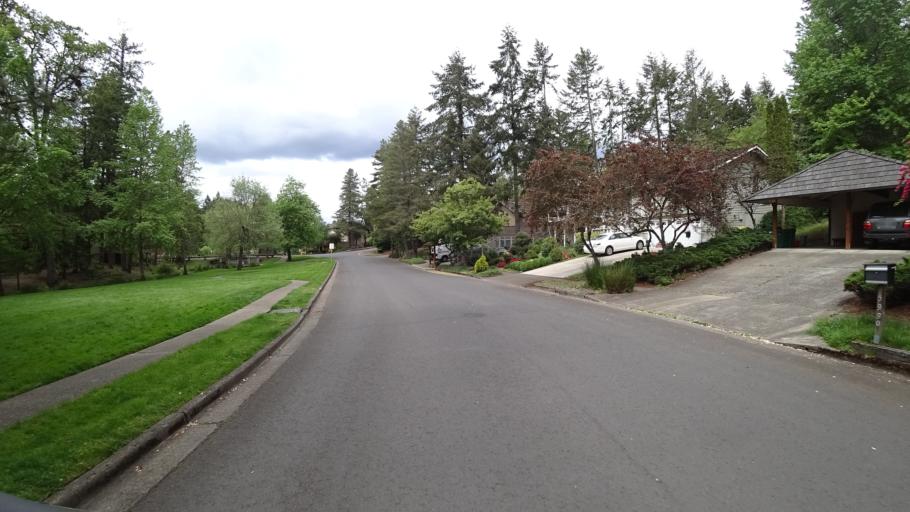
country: US
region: Oregon
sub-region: Washington County
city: Beaverton
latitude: 45.4765
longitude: -122.8307
